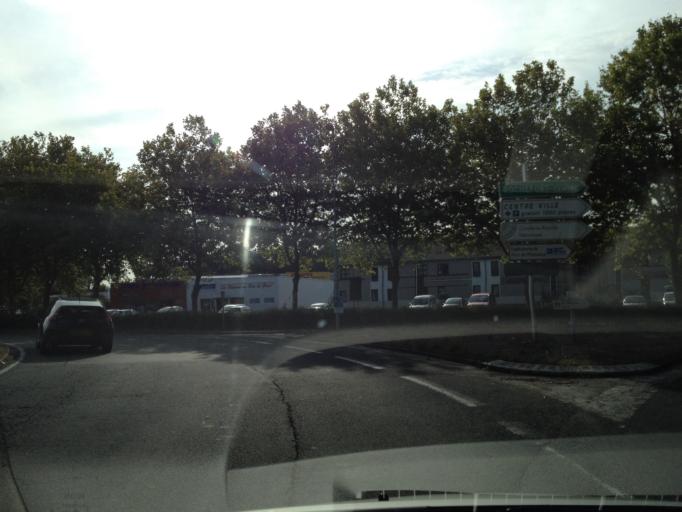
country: FR
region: Poitou-Charentes
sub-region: Departement de la Charente-Maritime
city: Rochefort
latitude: 45.9579
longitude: -0.9789
